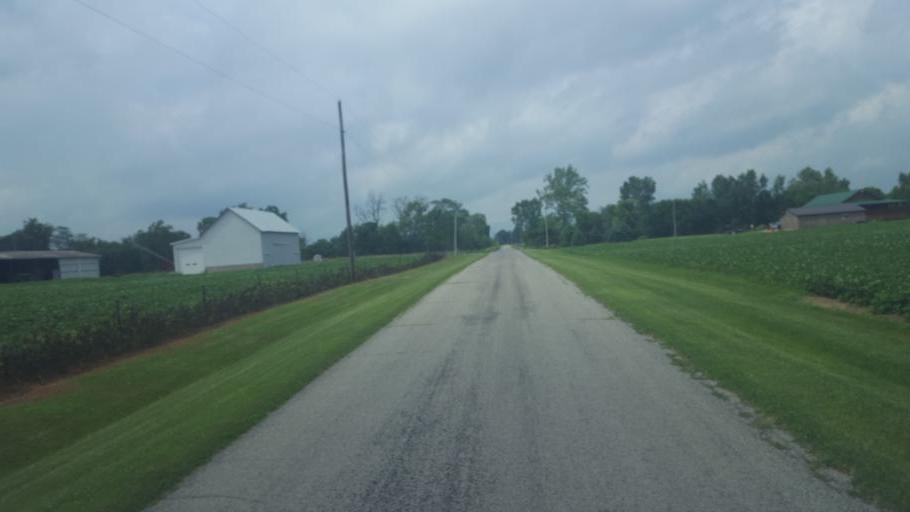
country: US
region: Ohio
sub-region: Union County
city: Richwood
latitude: 40.4748
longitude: -83.3282
